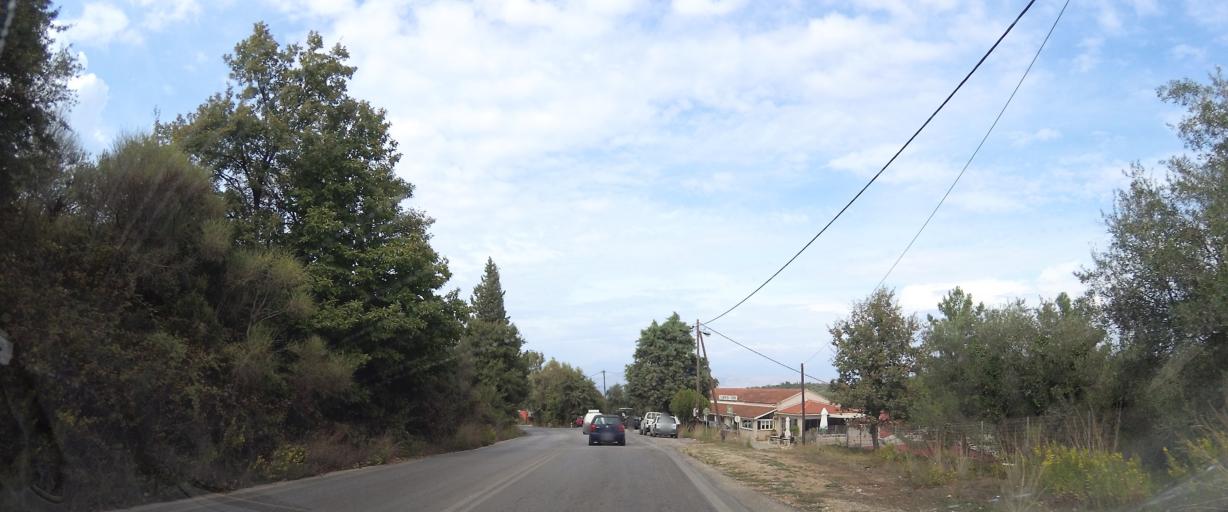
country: GR
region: Ionian Islands
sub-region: Nomos Kerkyras
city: Acharavi
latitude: 39.7626
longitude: 19.9324
